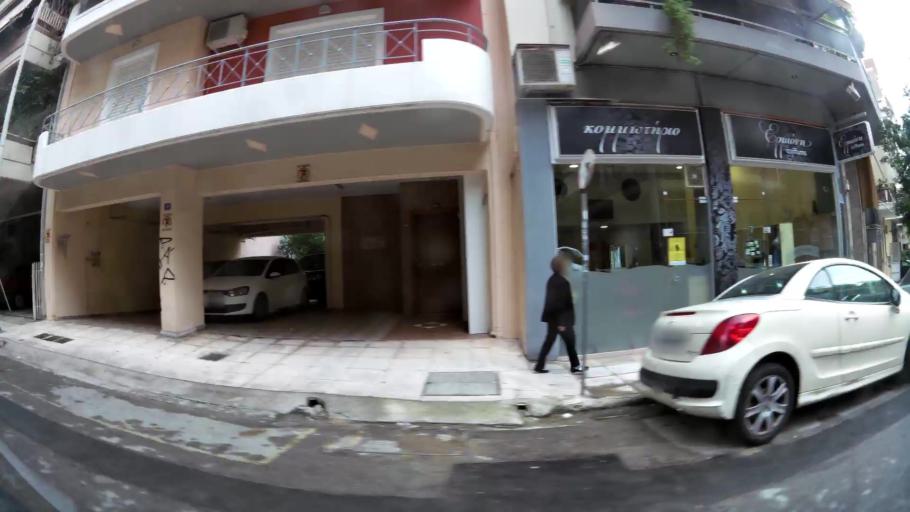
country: GR
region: Attica
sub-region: Nomarchia Athinas
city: Vyronas
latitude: 37.9602
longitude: 23.7588
